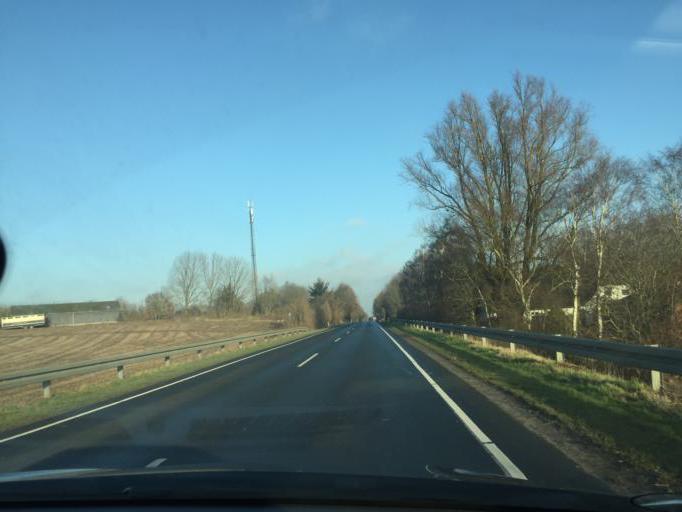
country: DK
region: South Denmark
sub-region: Faaborg-Midtfyn Kommune
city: Faaborg
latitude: 55.1889
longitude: 10.3085
